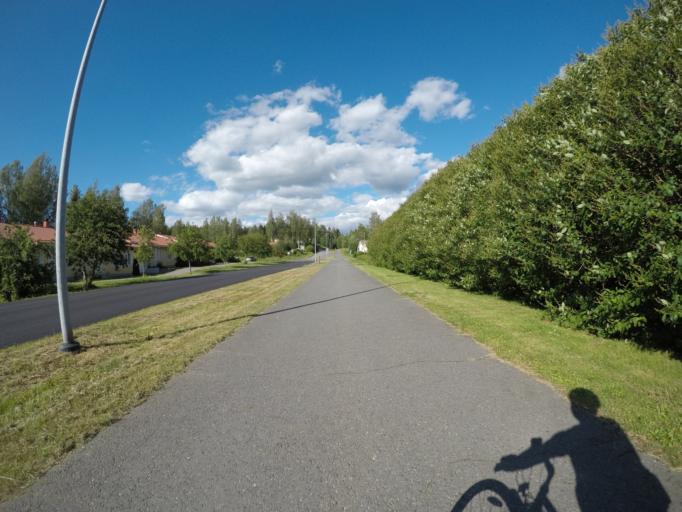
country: FI
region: Haeme
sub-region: Haemeenlinna
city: Haemeenlinna
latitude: 61.0202
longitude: 24.5188
